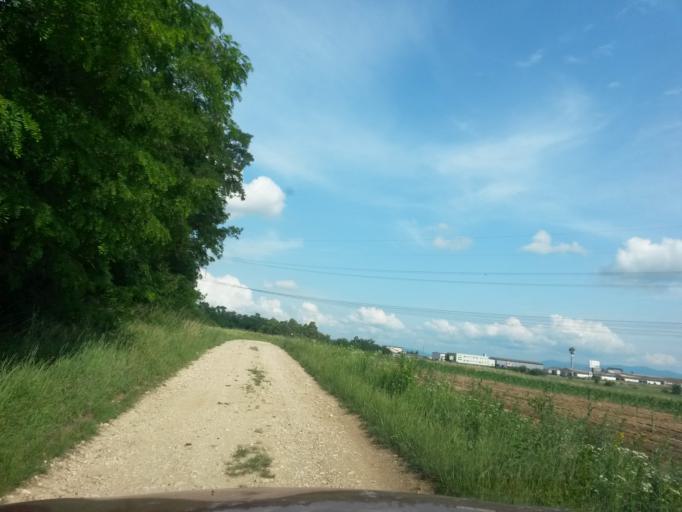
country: SK
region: Kosicky
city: Moldava nad Bodvou
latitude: 48.6087
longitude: 21.1057
